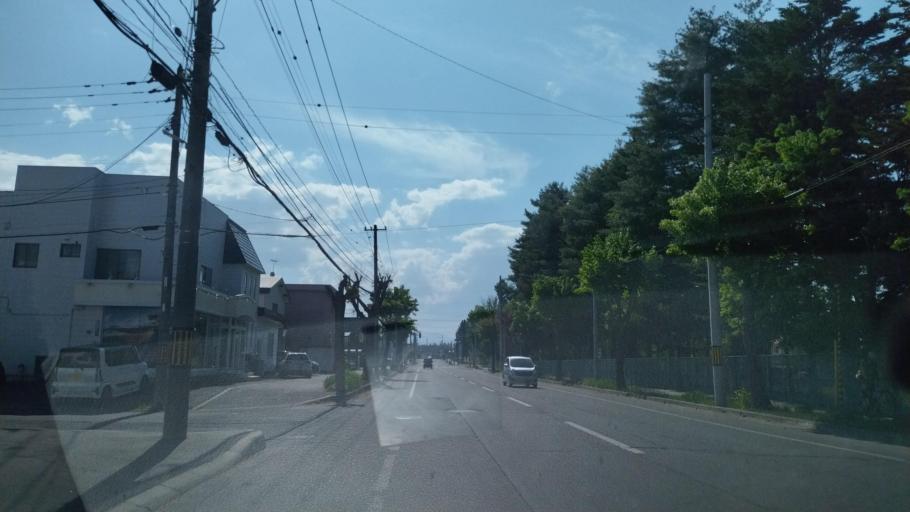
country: JP
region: Hokkaido
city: Obihiro
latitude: 42.9011
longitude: 143.1996
